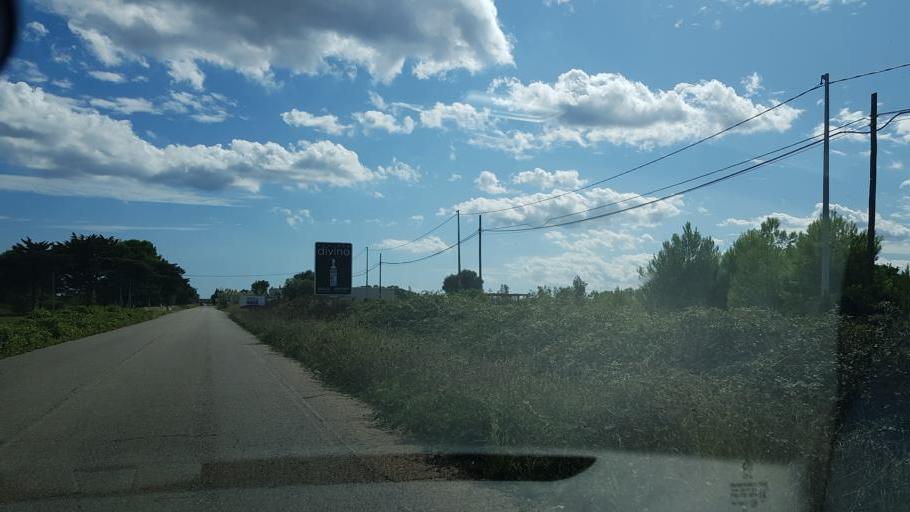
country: IT
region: Apulia
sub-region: Provincia di Lecce
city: Borgagne
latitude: 40.2649
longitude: 18.4321
